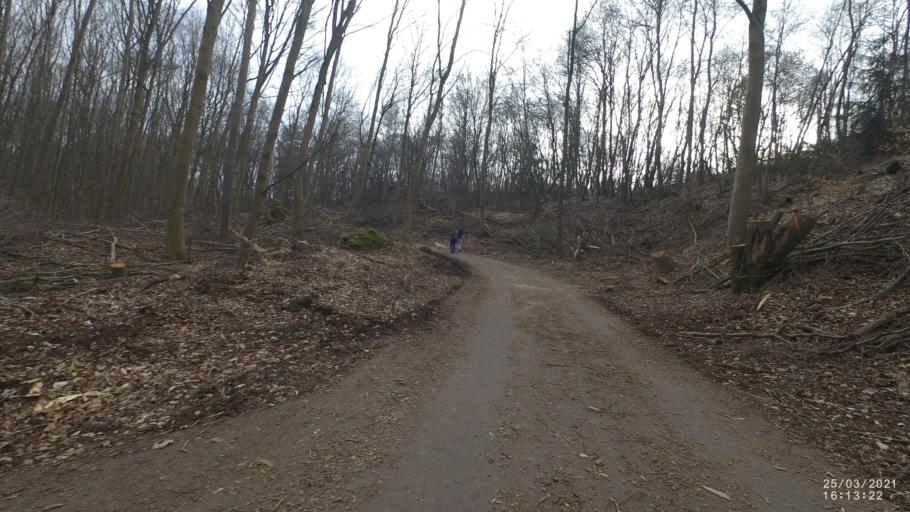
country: DE
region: Rheinland-Pfalz
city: Kottenheim
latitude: 50.3442
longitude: 7.2421
